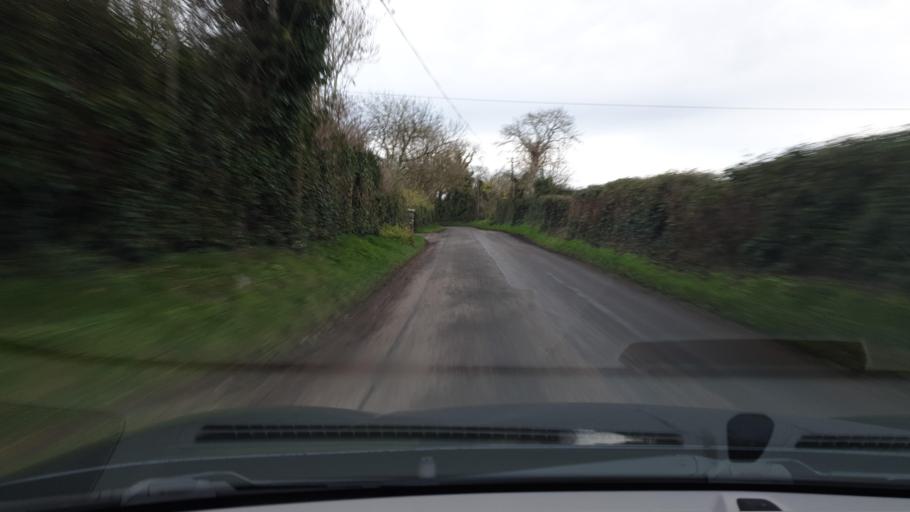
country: IE
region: Leinster
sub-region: An Mhi
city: Ashbourne
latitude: 53.5399
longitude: -6.3405
